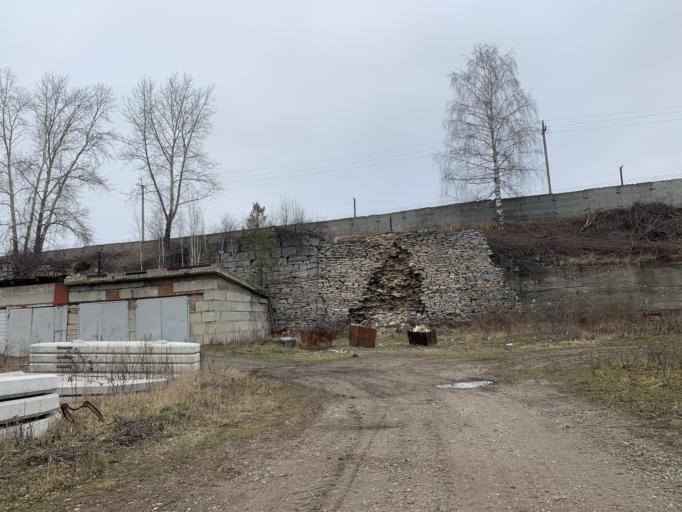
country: RU
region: Chelyabinsk
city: Nyazepetrovsk
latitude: 56.0547
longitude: 59.5914
